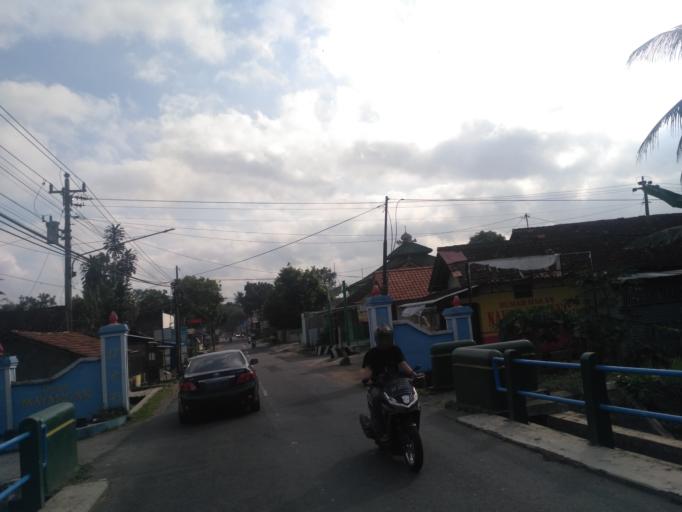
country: ID
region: Daerah Istimewa Yogyakarta
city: Melati
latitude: -7.7542
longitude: 110.3471
